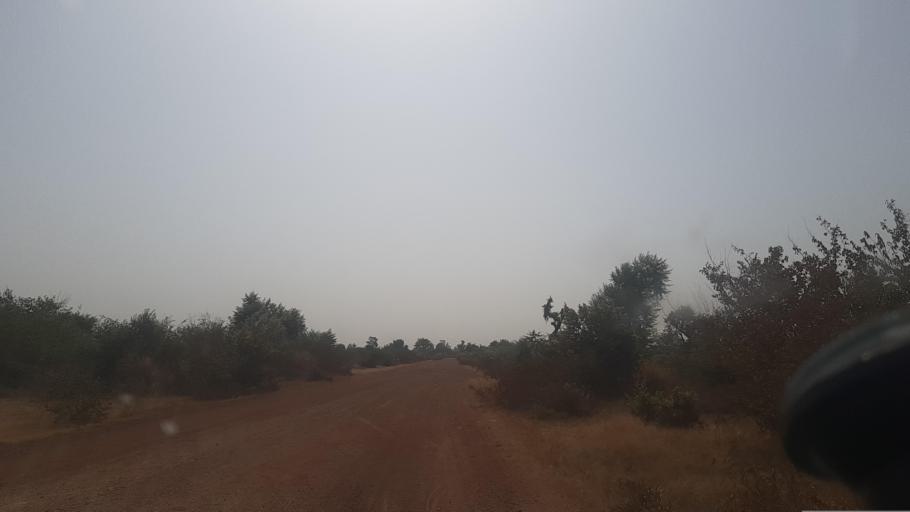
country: ML
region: Segou
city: Baroueli
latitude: 13.0619
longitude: -6.4737
